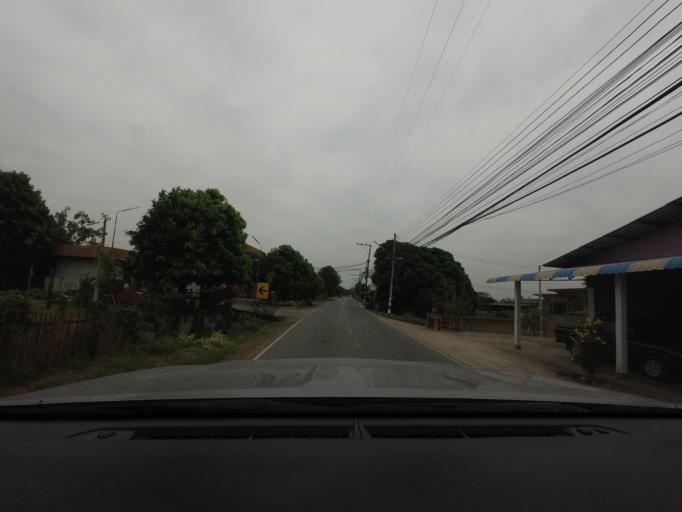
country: TH
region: Lamphun
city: Lamphun
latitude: 18.6259
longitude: 99.0180
